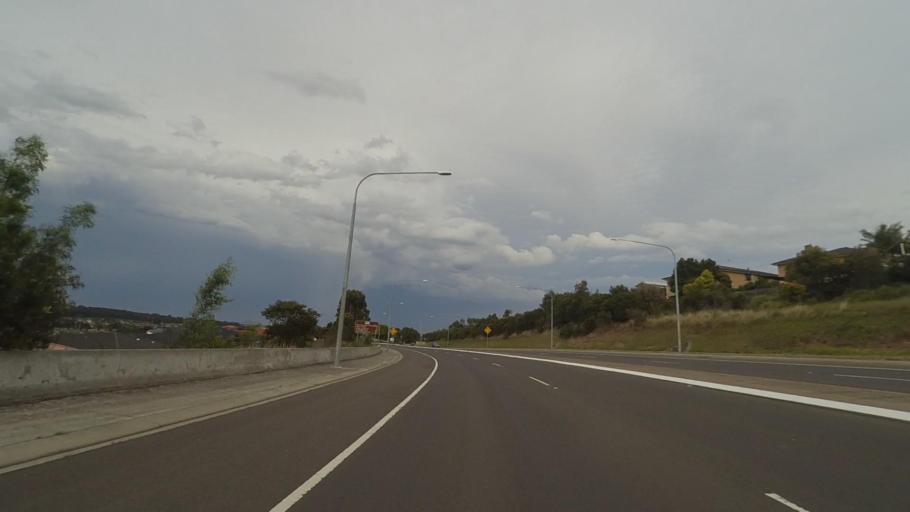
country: AU
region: New South Wales
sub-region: Shellharbour
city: Flinders
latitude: -34.5896
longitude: 150.8512
